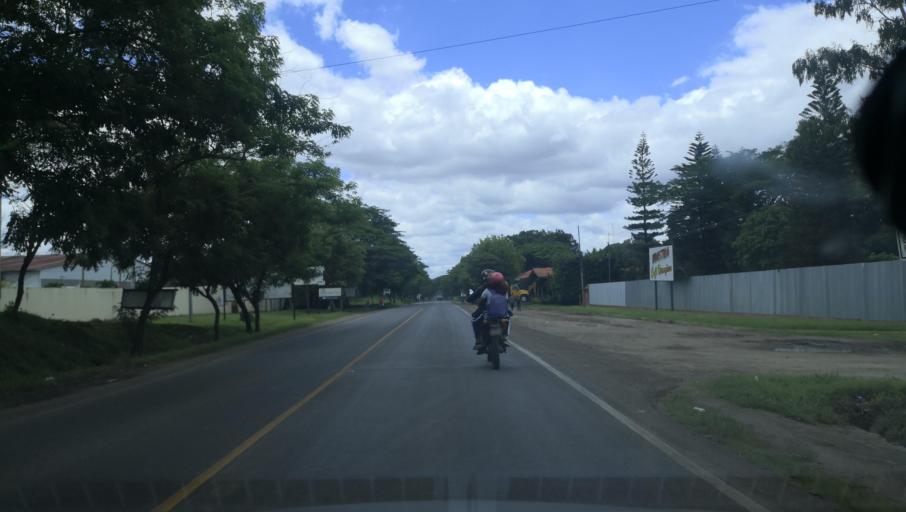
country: NI
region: Esteli
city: Esteli
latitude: 13.1234
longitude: -86.3633
